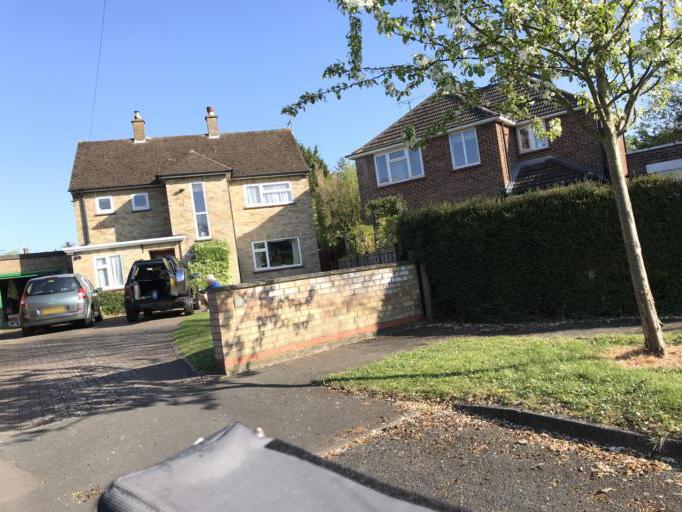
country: GB
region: England
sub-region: Cambridgeshire
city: Cambridge
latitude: 52.1791
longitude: 0.1589
